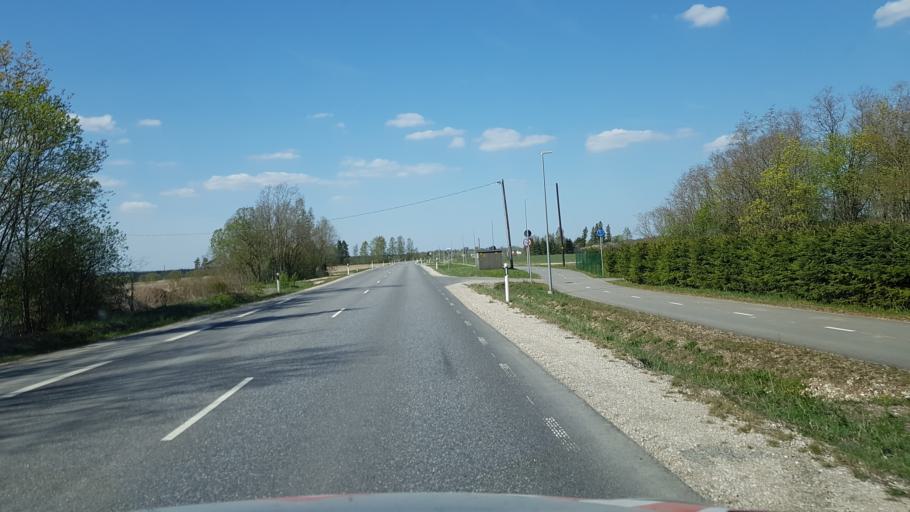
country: EE
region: Harju
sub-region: Raasiku vald
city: Arukula
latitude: 59.1896
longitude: 25.1135
